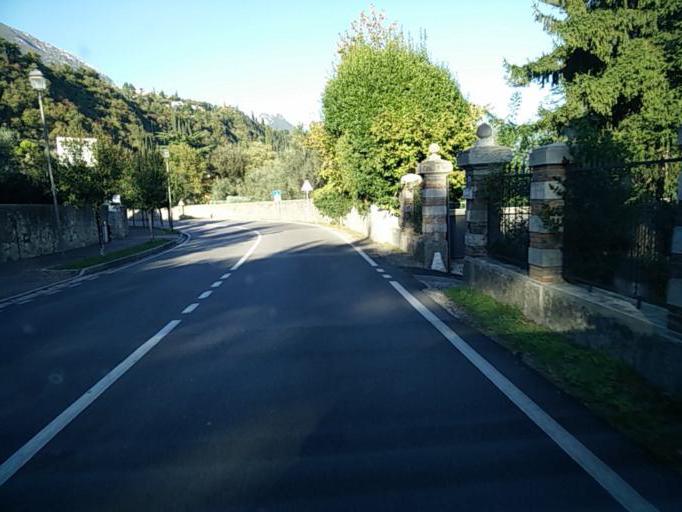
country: IT
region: Lombardy
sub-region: Provincia di Brescia
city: Gardone Riviera
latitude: 45.6274
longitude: 10.5863
